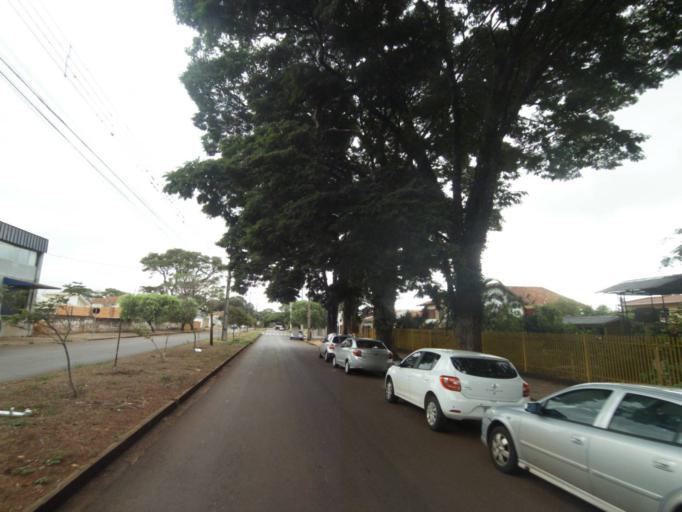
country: BR
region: Parana
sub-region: Campo Mourao
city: Campo Mourao
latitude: -24.0445
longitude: -52.3709
